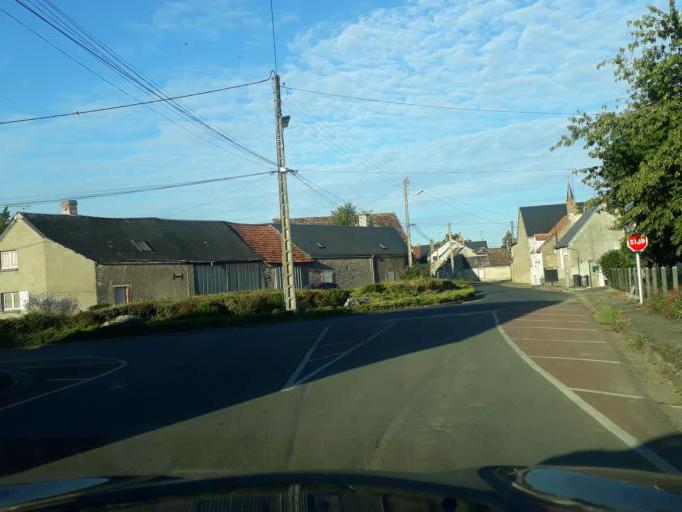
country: FR
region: Centre
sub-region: Departement du Loir-et-Cher
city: Ouzouer-le-Marche
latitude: 47.9692
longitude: 1.5410
